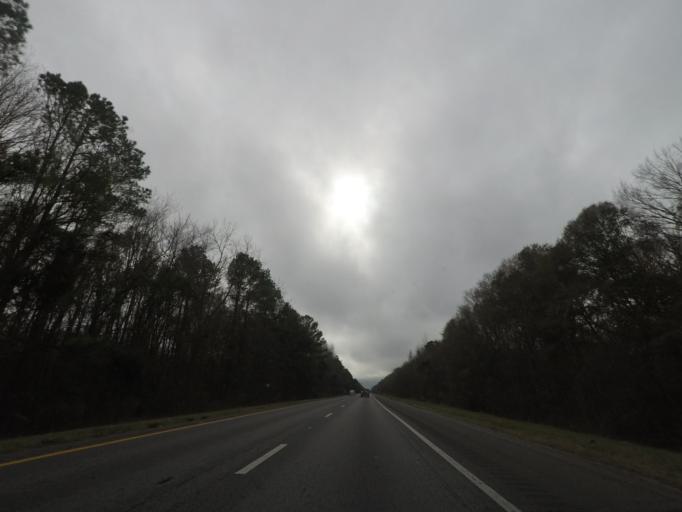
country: US
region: South Carolina
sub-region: Orangeburg County
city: Holly Hill
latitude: 33.3534
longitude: -80.5297
